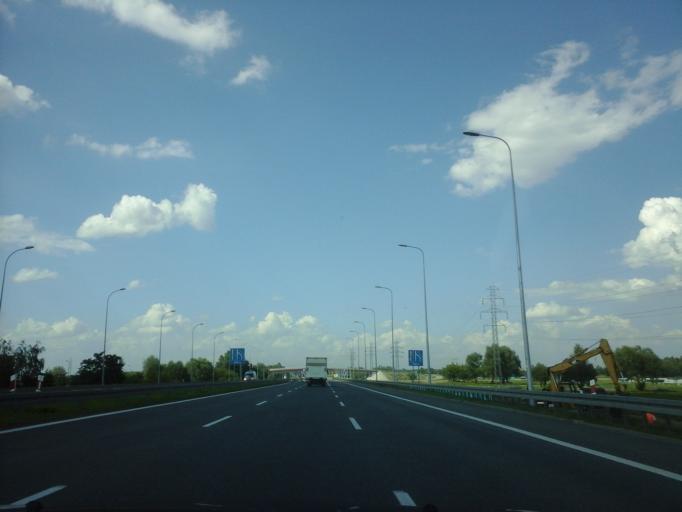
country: PL
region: Lesser Poland Voivodeship
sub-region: Powiat wielicki
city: Kokotow
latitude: 50.0264
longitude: 20.0627
